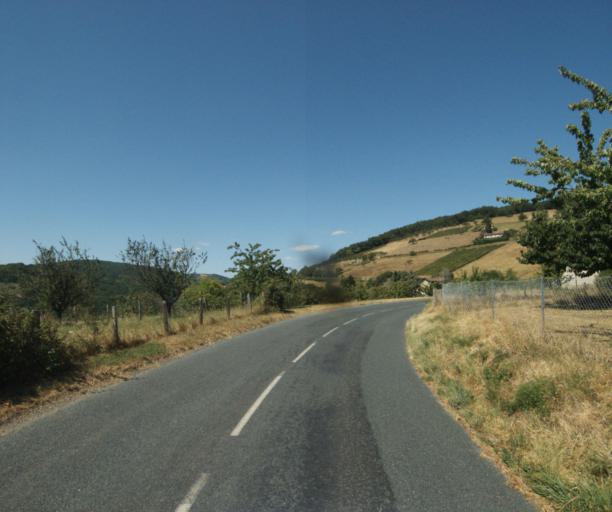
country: FR
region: Rhone-Alpes
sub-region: Departement du Rhone
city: Bessenay
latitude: 45.7929
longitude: 4.5433
